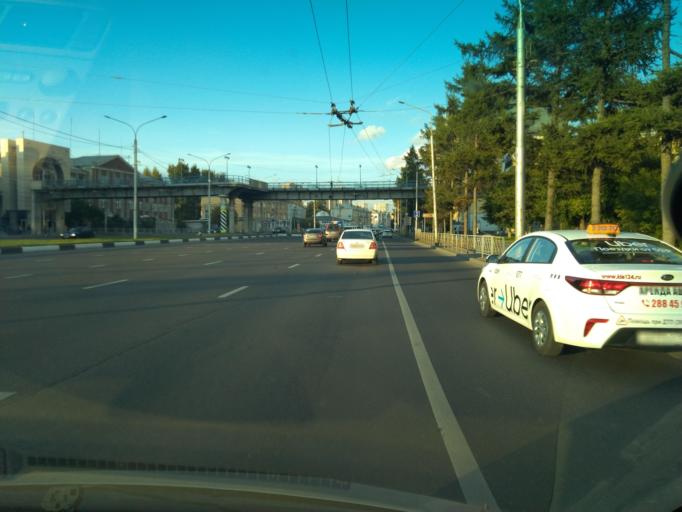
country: RU
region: Krasnoyarskiy
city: Krasnoyarsk
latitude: 56.0251
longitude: 92.9055
